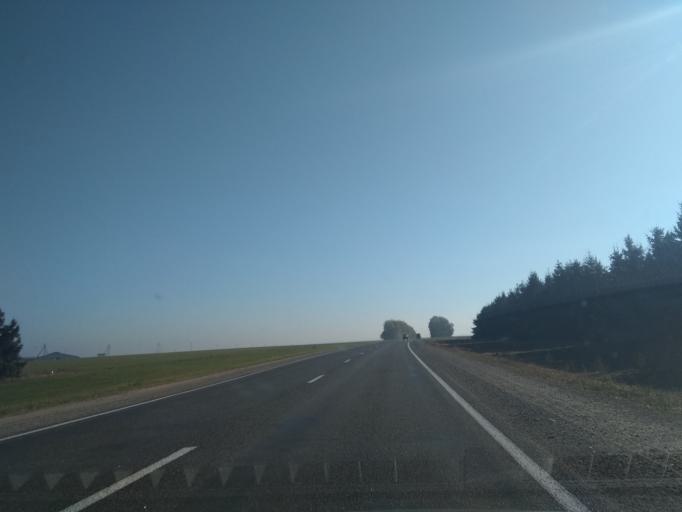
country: BY
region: Grodnenskaya
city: Slonim
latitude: 53.1230
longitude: 25.0831
